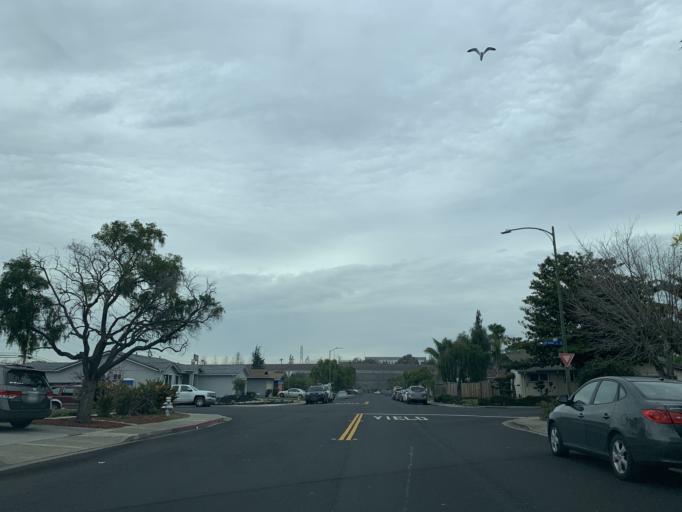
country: US
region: California
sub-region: Santa Clara County
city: Mountain View
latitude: 37.4063
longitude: -122.0734
